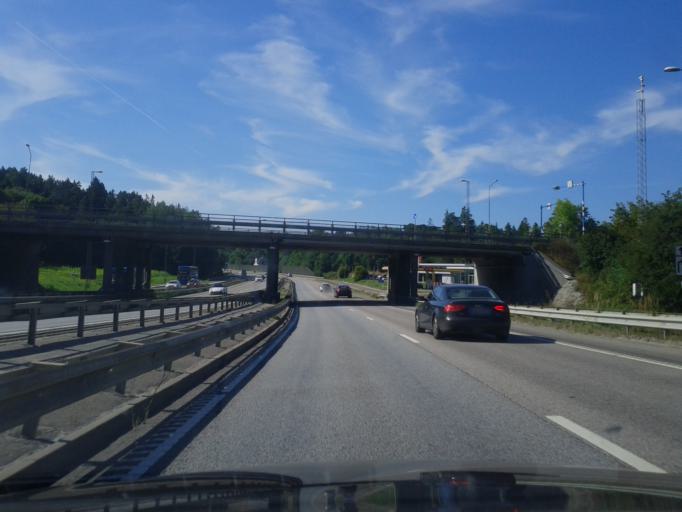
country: SE
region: Stockholm
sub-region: Taby Kommun
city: Taby
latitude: 59.4349
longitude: 18.0697
